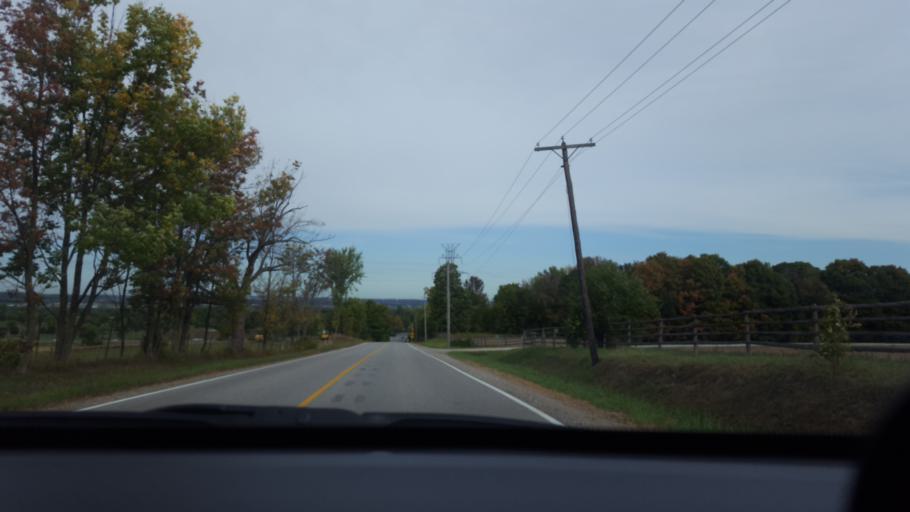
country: CA
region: Ontario
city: Newmarket
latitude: 44.0327
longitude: -79.5552
